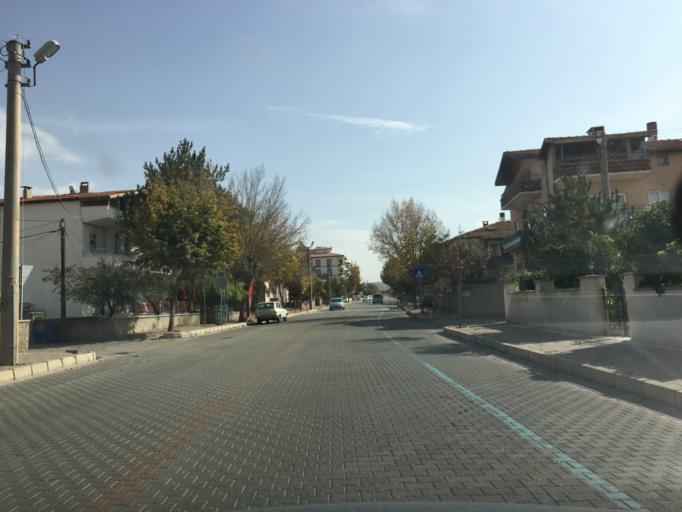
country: TR
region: Nevsehir
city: Avanos
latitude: 38.7090
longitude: 34.8502
